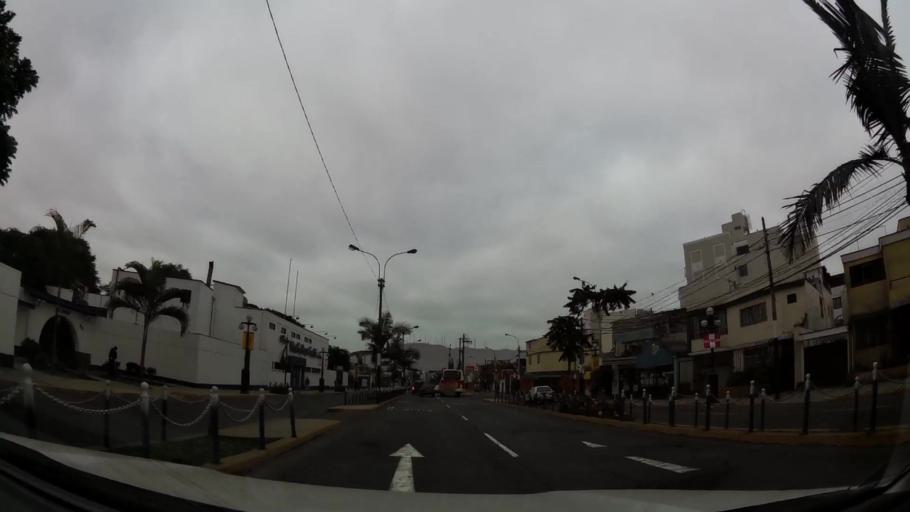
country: PE
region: Lima
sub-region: Lima
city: Surco
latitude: -12.1570
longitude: -77.0230
